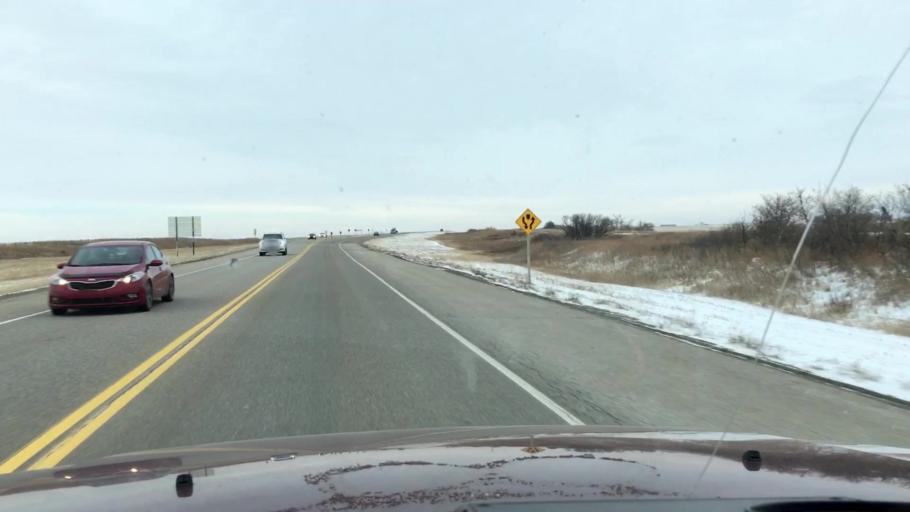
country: CA
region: Saskatchewan
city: Moose Jaw
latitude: 50.8448
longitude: -105.5549
